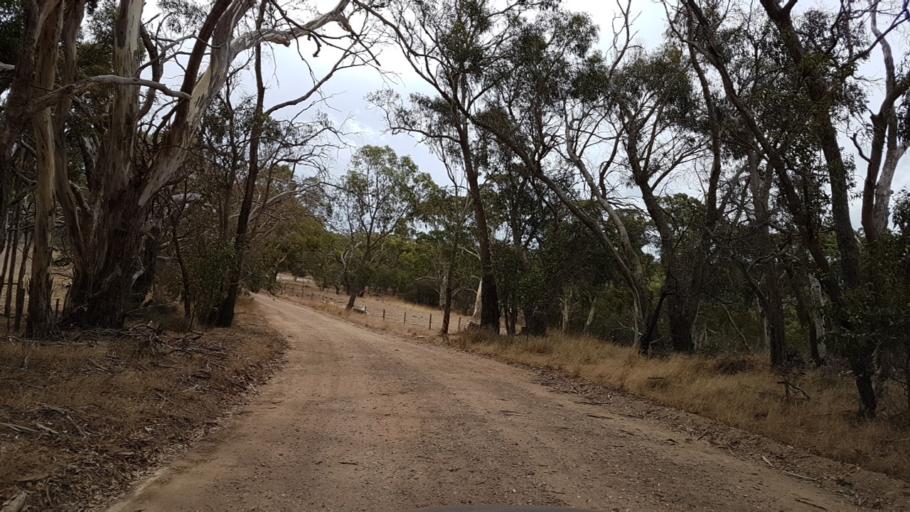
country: AU
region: South Australia
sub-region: Adelaide Hills
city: Birdwood
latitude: -34.7709
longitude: 138.9909
